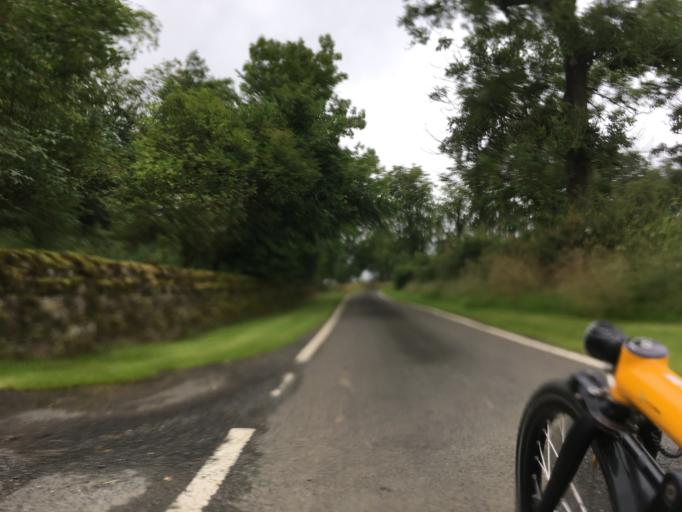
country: GB
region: Scotland
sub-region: West Lothian
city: West Calder
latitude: 55.8473
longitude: -3.5374
